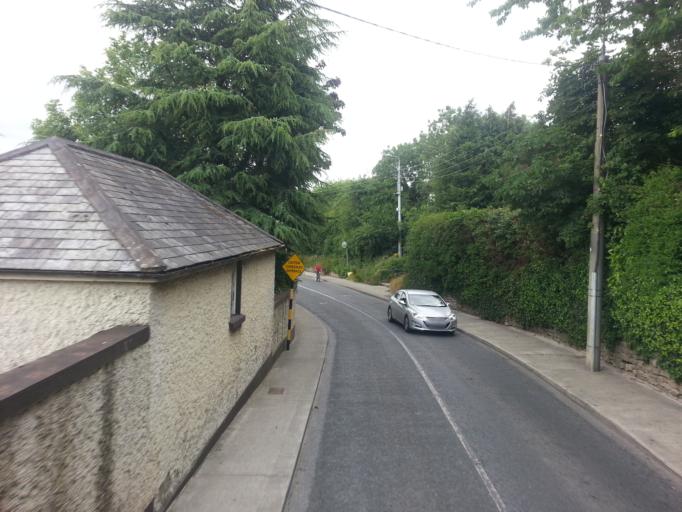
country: IE
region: Leinster
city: Sandyford
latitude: 53.2533
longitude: -6.2144
